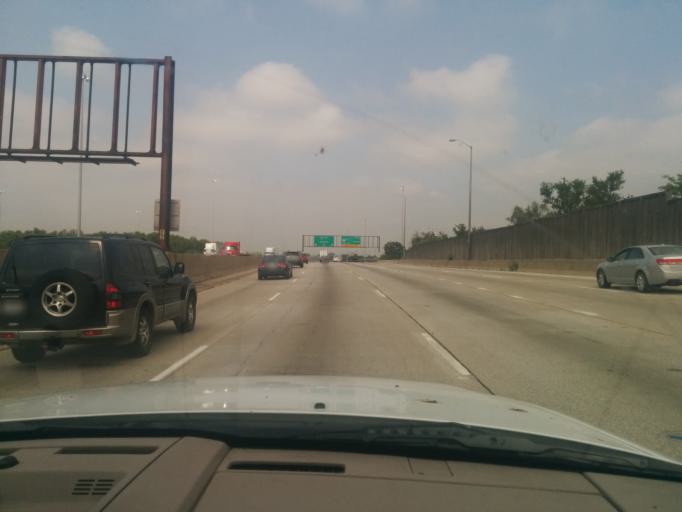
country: US
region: Illinois
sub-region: DuPage County
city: Elmhurst
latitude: 41.9137
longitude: -87.9378
